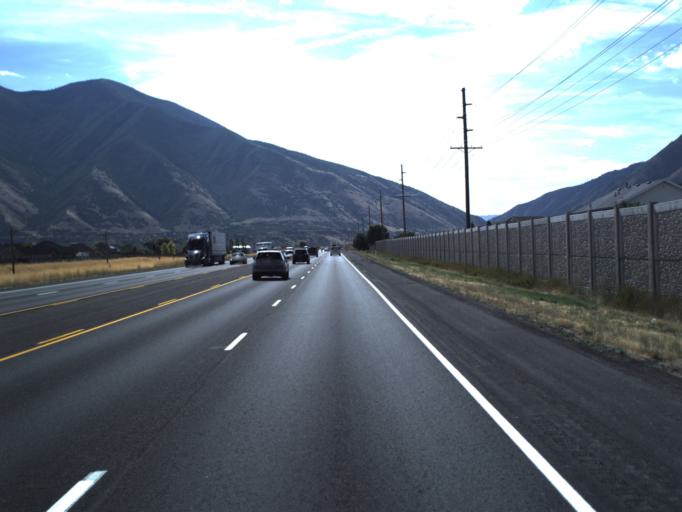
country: US
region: Utah
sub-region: Utah County
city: Spanish Fork
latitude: 40.1056
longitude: -111.6243
